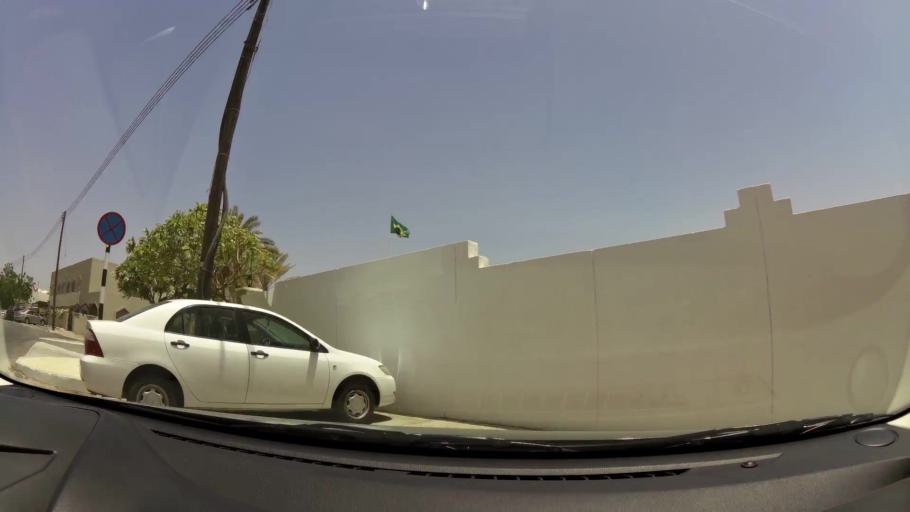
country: OM
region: Muhafazat Masqat
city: Muscat
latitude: 23.6250
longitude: 58.4956
